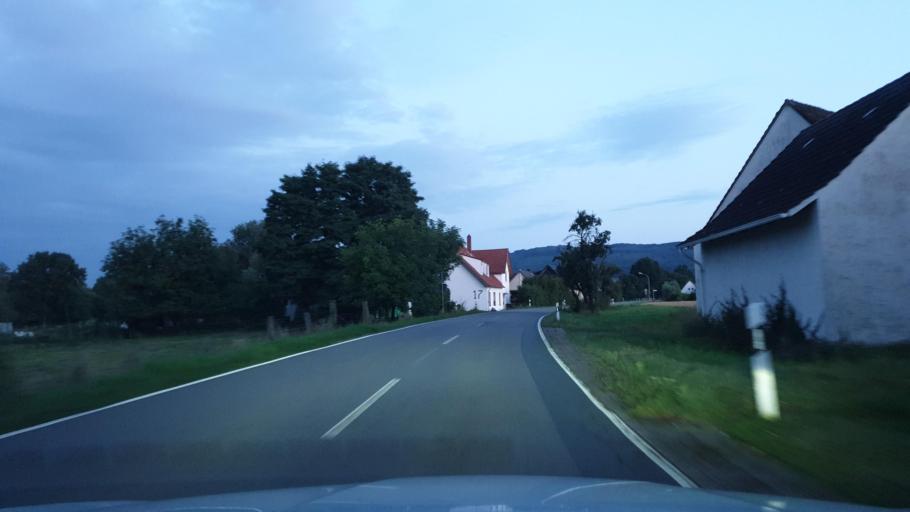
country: DE
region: North Rhine-Westphalia
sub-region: Regierungsbezirk Detmold
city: Huellhorst
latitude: 52.3252
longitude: 8.6676
